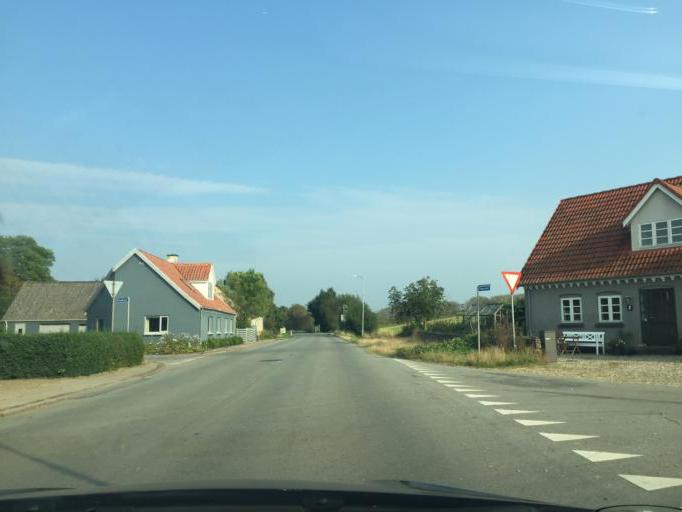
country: DK
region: South Denmark
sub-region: Faaborg-Midtfyn Kommune
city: Arslev
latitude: 55.2817
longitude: 10.4917
